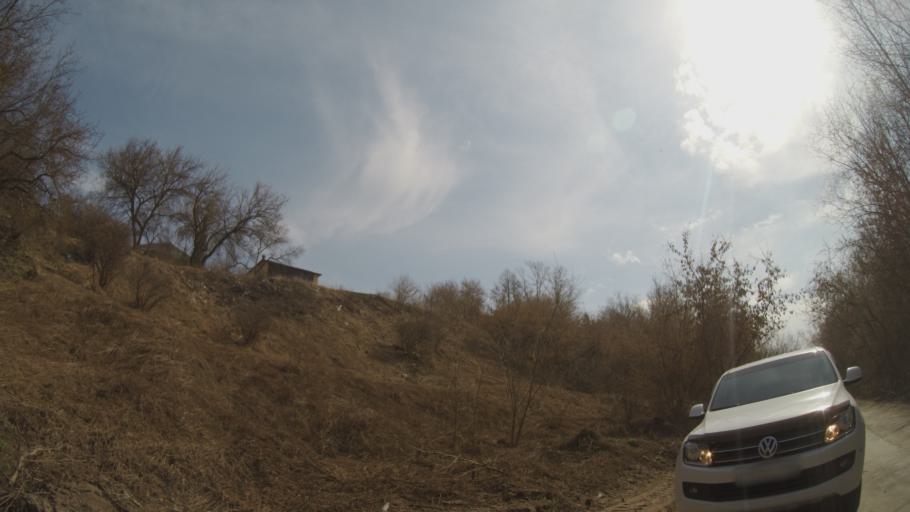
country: RU
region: Nizjnij Novgorod
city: Vyyezdnoye
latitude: 55.3886
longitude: 43.8098
